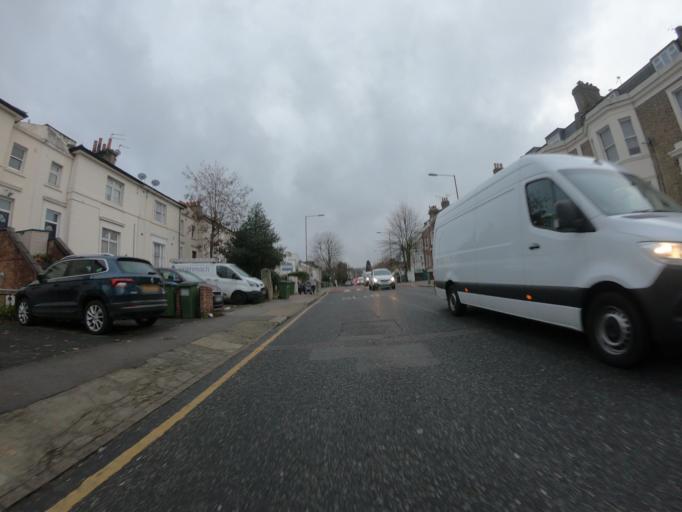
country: GB
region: England
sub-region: Greater London
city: Woolwich
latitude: 51.4846
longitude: 0.0733
